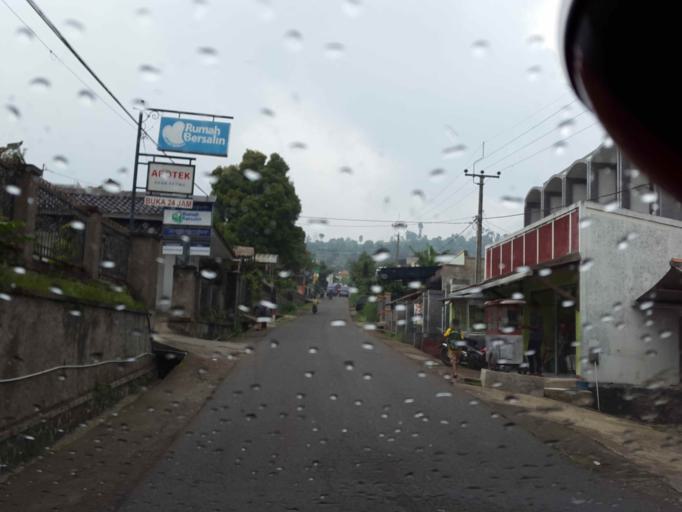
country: ID
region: West Java
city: Lembang
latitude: -6.8308
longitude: 107.5745
